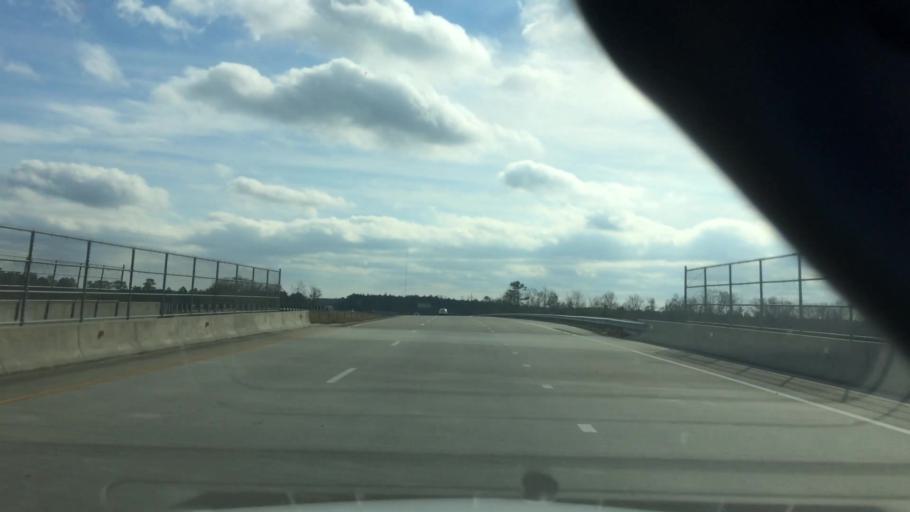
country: US
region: North Carolina
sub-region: Brunswick County
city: Leland
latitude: 34.2576
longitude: -78.0799
